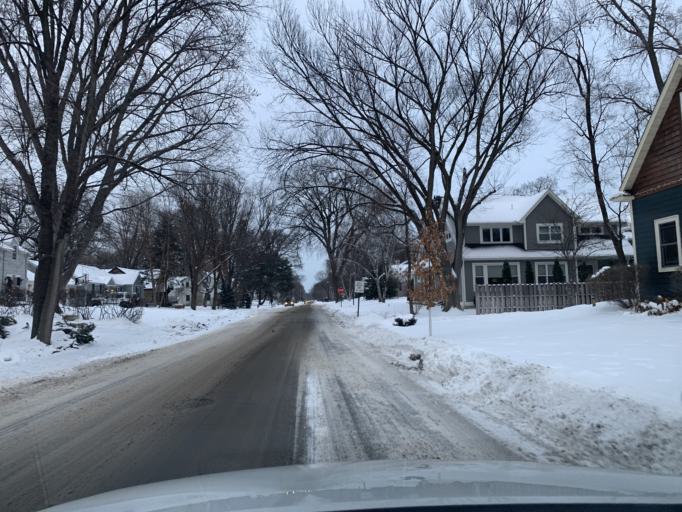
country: US
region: Minnesota
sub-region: Hennepin County
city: Saint Louis Park
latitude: 44.9269
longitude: -93.3397
